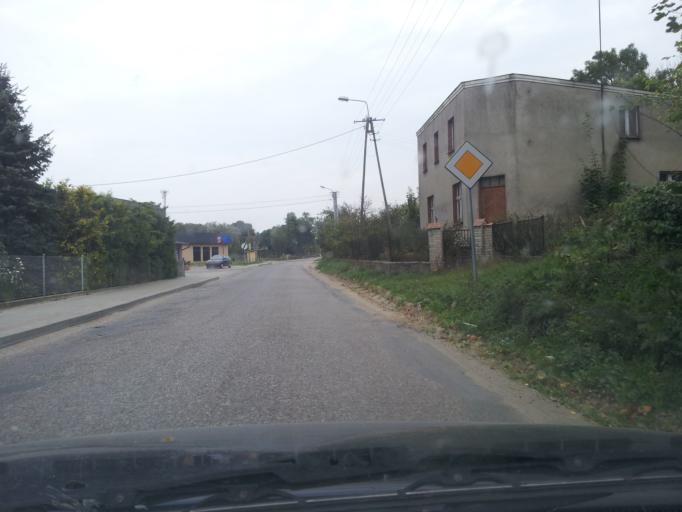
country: PL
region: Kujawsko-Pomorskie
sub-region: Powiat brodnicki
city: Brzozie
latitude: 53.3240
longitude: 19.7178
